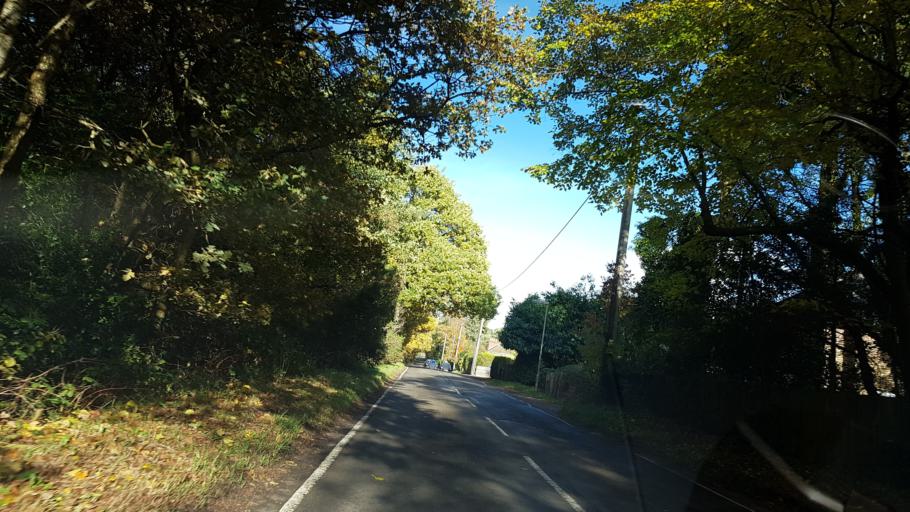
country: GB
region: England
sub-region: Surrey
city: Elstead
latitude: 51.1703
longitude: -0.7144
